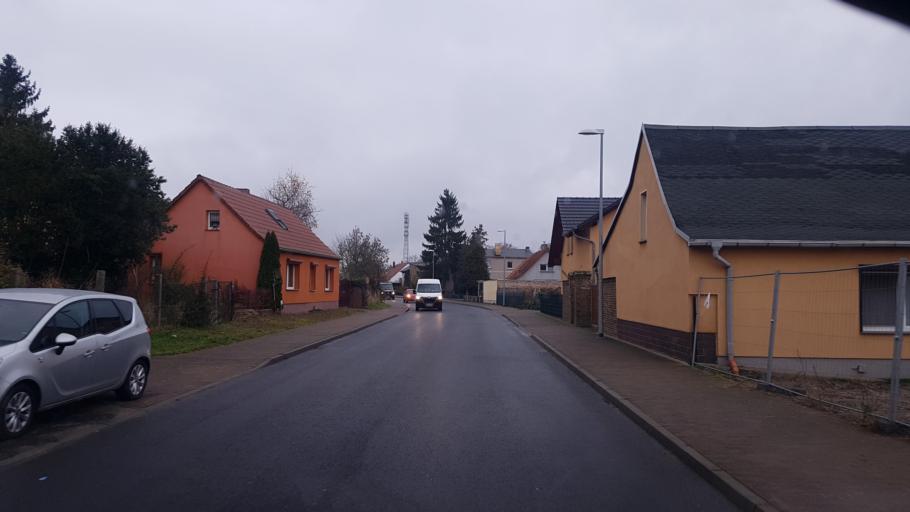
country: DE
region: Brandenburg
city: Brandenburg an der Havel
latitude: 52.4375
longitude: 12.6303
